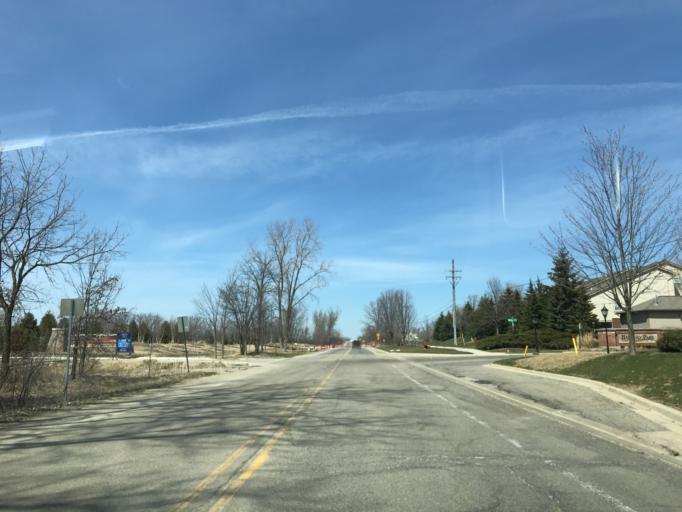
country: US
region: Michigan
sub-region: Washtenaw County
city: Ann Arbor
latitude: 42.3194
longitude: -83.7077
